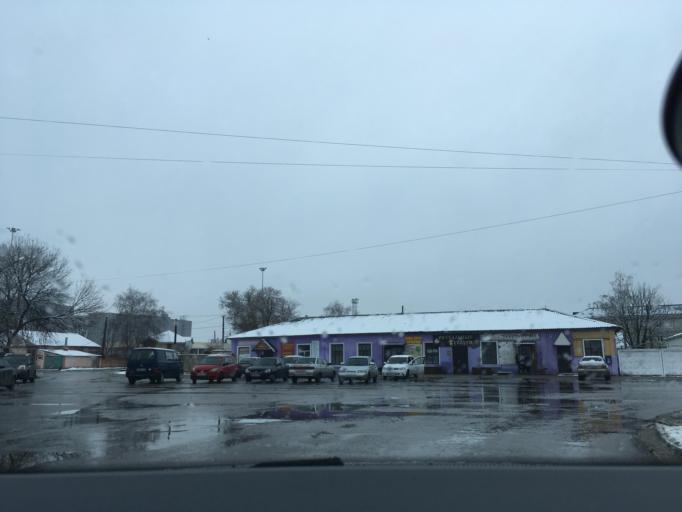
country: RU
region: Belgorod
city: Valuyki
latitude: 50.2020
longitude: 38.1213
